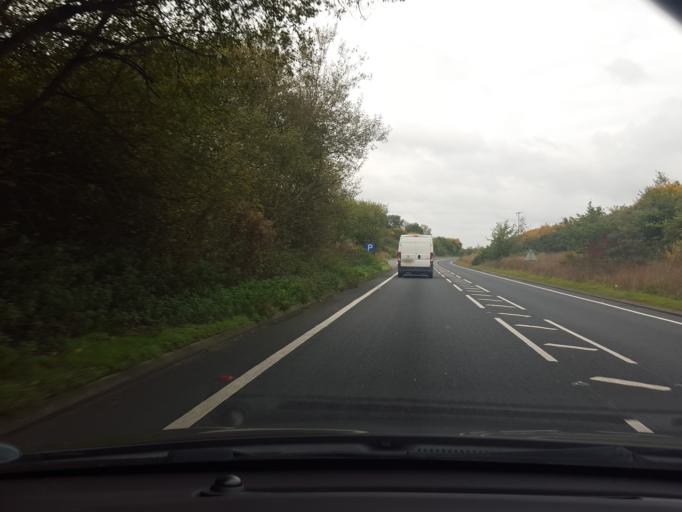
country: GB
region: England
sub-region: Essex
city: Little Clacton
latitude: 51.8456
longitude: 1.1069
